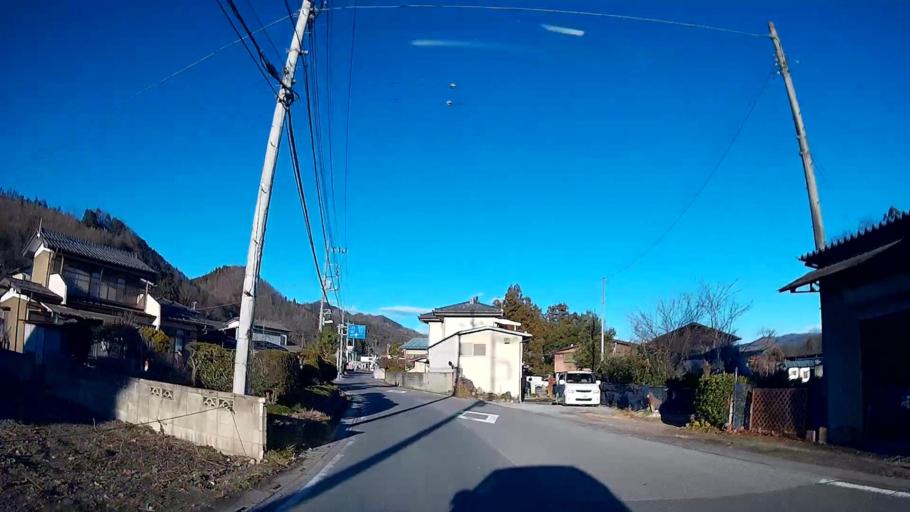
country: JP
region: Saitama
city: Chichibu
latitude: 36.0468
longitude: 139.0395
